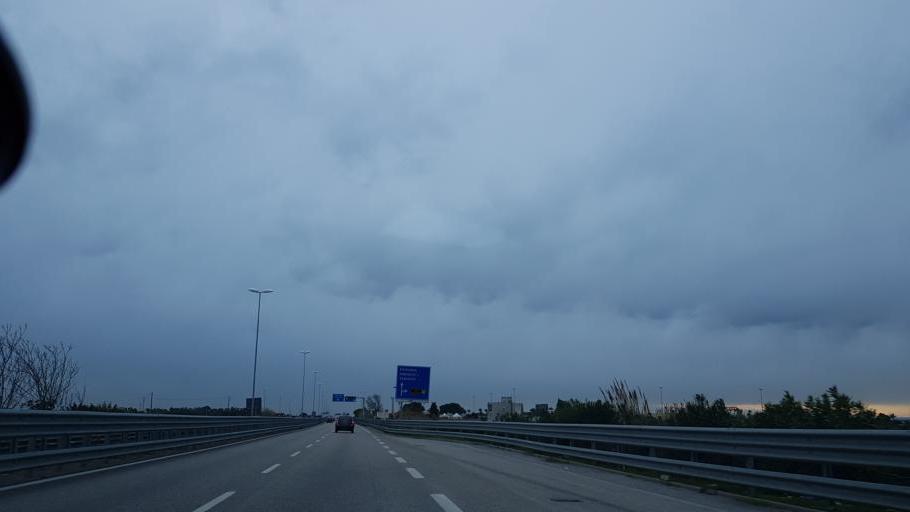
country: IT
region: Apulia
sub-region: Provincia di Brindisi
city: Brindisi
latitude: 40.6207
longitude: 17.9101
